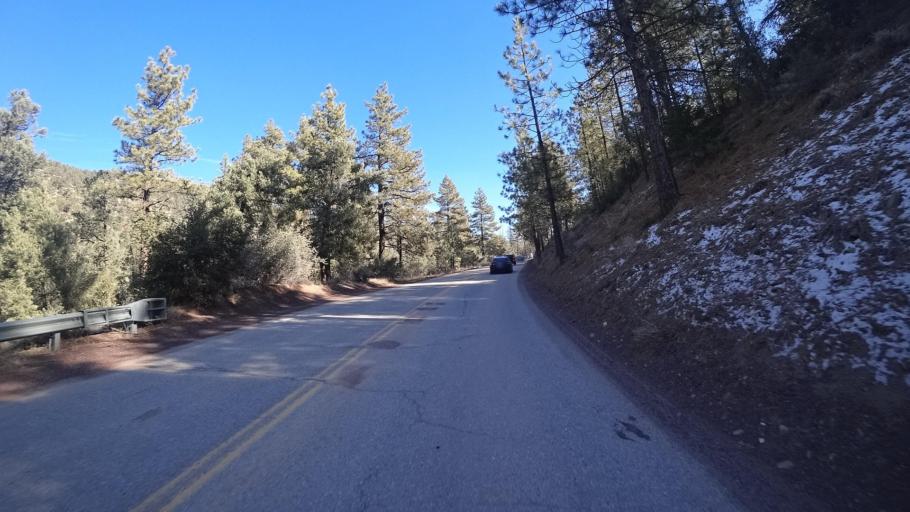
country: US
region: California
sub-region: Kern County
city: Pine Mountain Club
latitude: 34.8494
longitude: -119.1004
